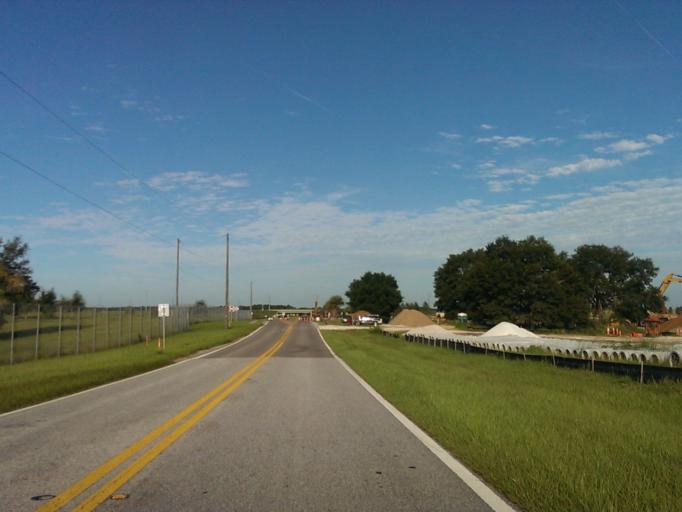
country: US
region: Florida
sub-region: Polk County
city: Citrus Ridge
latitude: 28.4199
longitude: -81.6245
